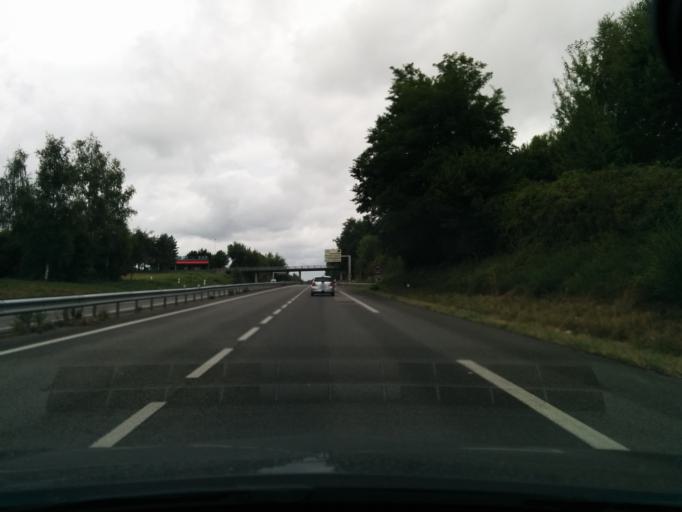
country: FR
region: Limousin
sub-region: Departement de la Haute-Vienne
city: Saint-Germain-les-Belles
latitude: 45.6238
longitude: 1.4432
